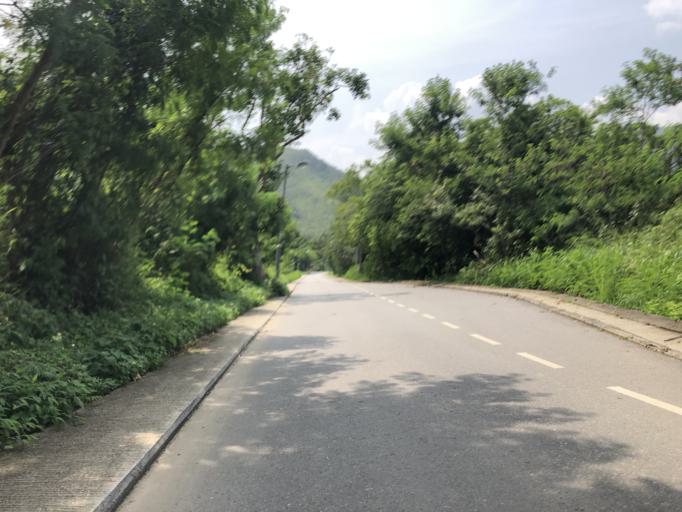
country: CN
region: Guangdong
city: Haishan
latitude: 22.5254
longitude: 114.2130
